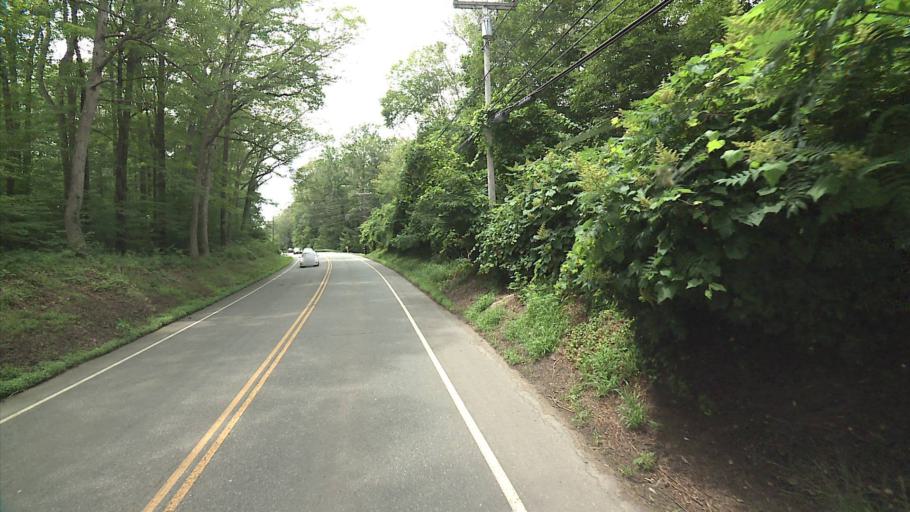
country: US
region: Connecticut
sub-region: New Haven County
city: North Branford
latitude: 41.3562
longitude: -72.7065
